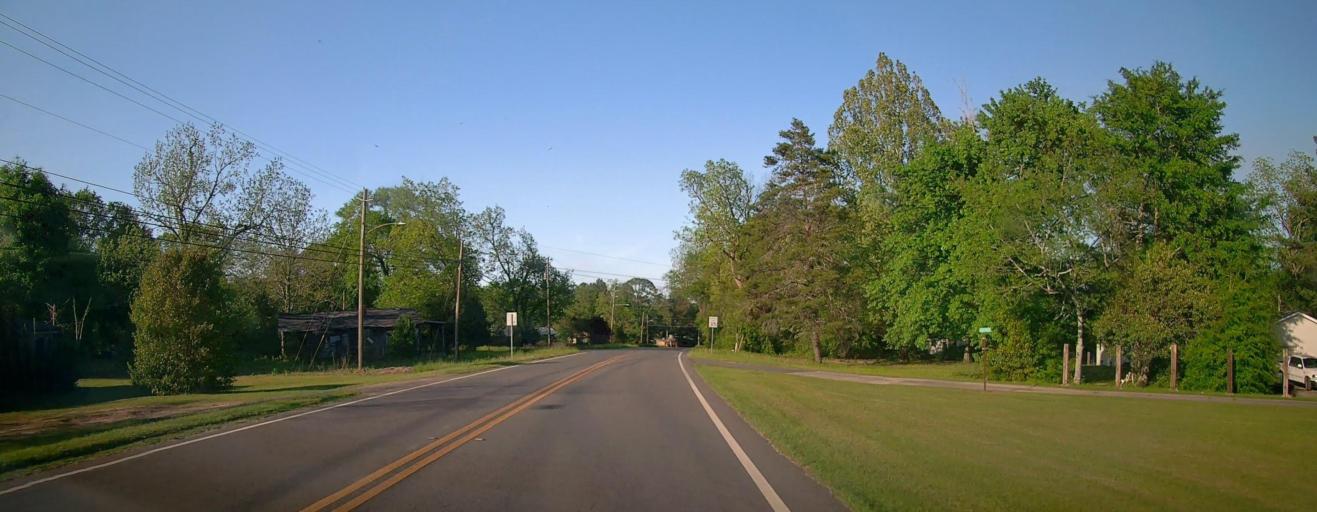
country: US
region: Georgia
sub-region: Macon County
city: Oglethorpe
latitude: 32.2887
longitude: -84.0676
